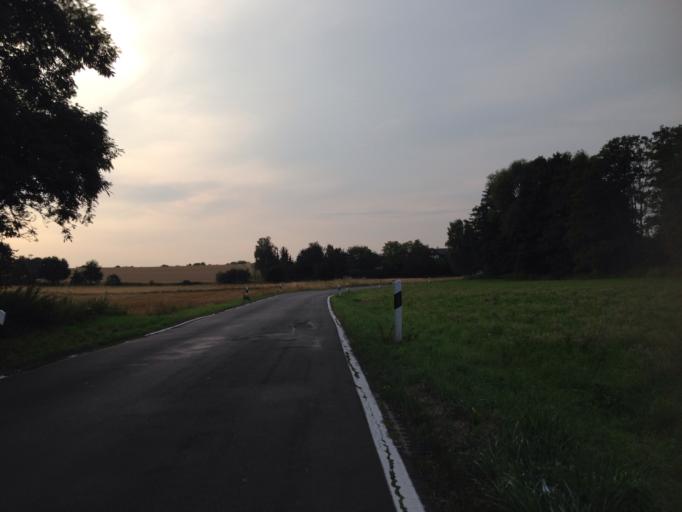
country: DE
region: Hesse
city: Allendorf an der Lahn
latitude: 50.5551
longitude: 8.6144
